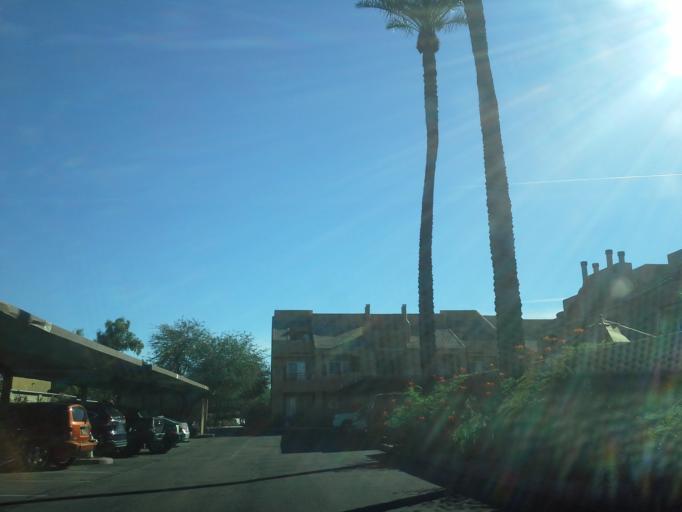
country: US
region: Arizona
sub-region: Maricopa County
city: Paradise Valley
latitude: 33.6256
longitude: -111.9984
